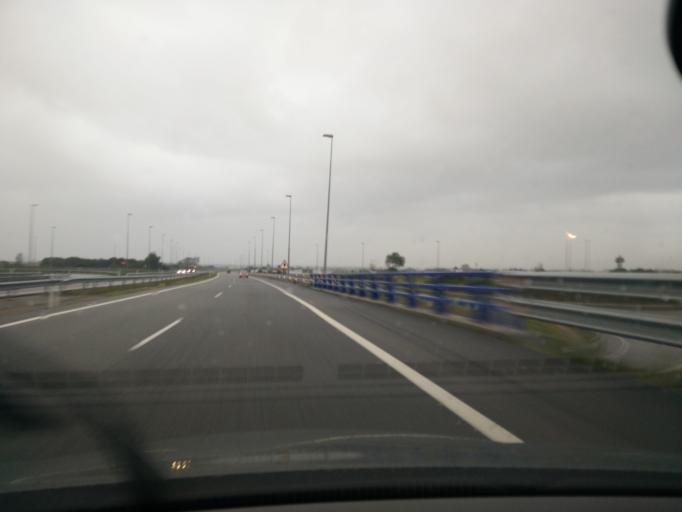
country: ES
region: Asturias
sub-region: Province of Asturias
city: Figueras
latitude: 43.5434
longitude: -7.0221
